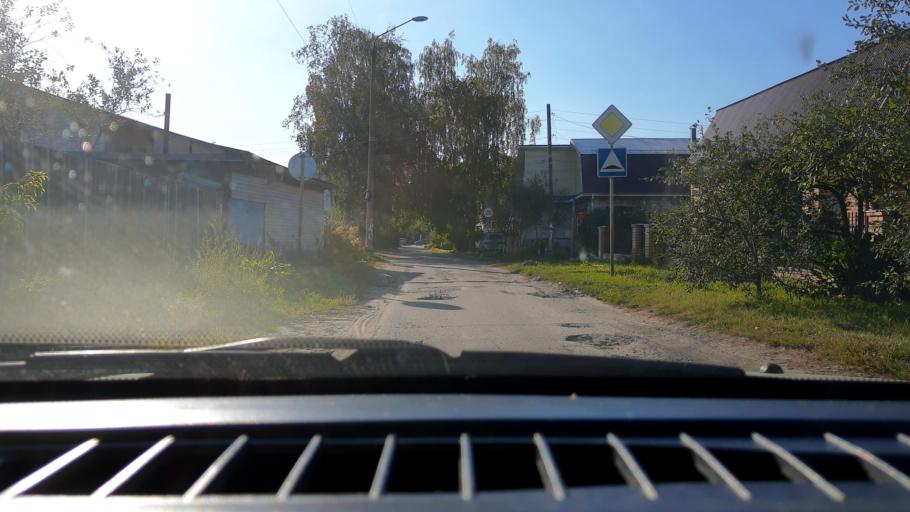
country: RU
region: Nizjnij Novgorod
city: Bor
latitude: 56.3777
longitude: 44.0297
